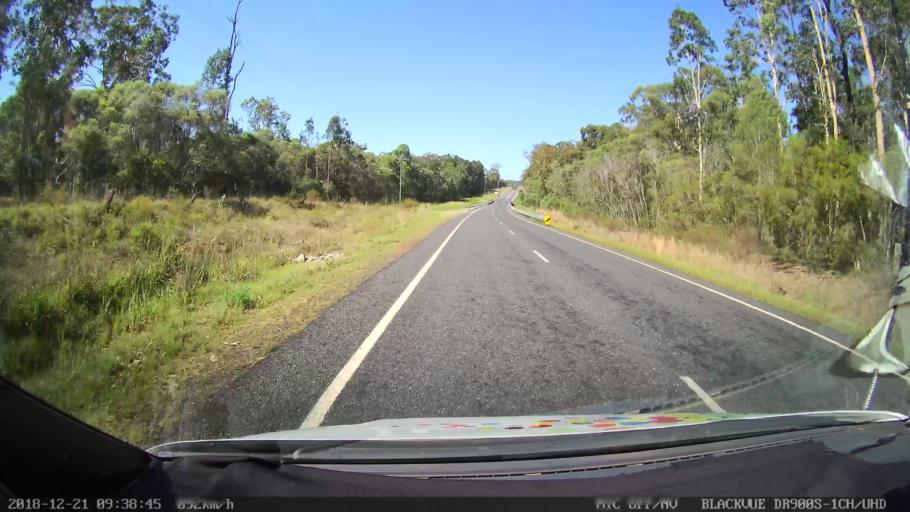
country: AU
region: New South Wales
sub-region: Clarence Valley
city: Grafton
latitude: -29.5534
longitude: 152.9801
